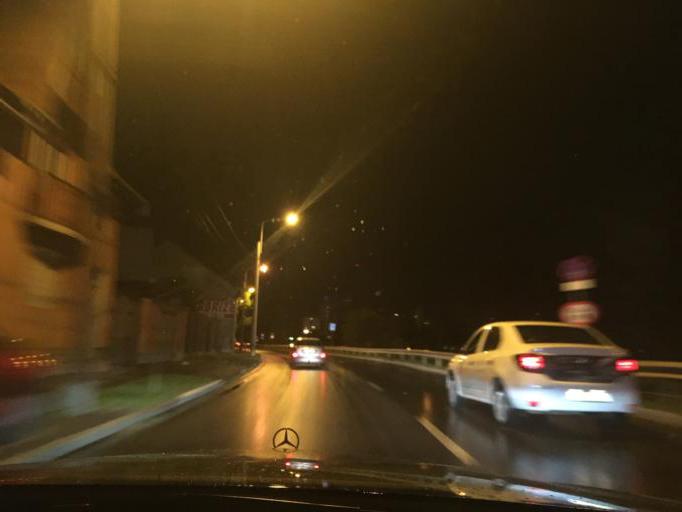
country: RO
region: Bihor
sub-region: Comuna Biharea
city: Oradea
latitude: 47.0537
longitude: 21.9470
